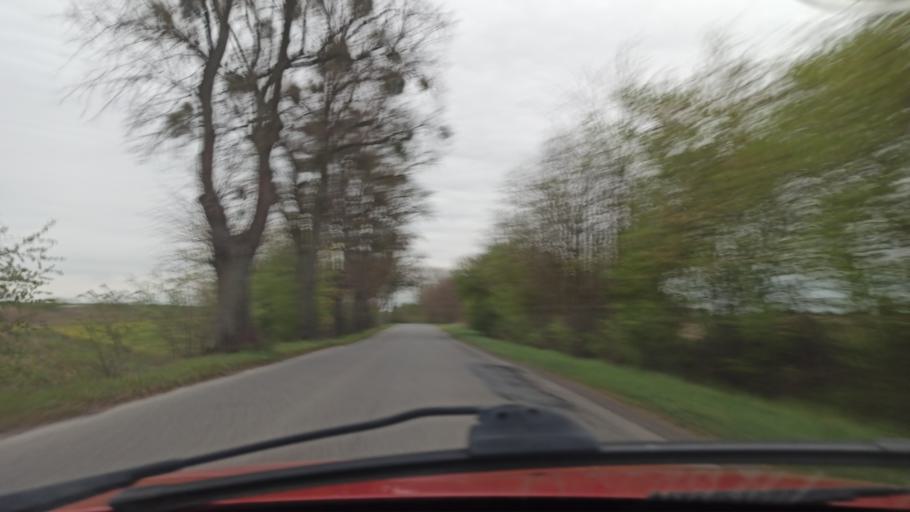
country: PL
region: Pomeranian Voivodeship
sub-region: Powiat kwidzynski
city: Gardeja
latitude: 53.5721
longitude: 18.9830
